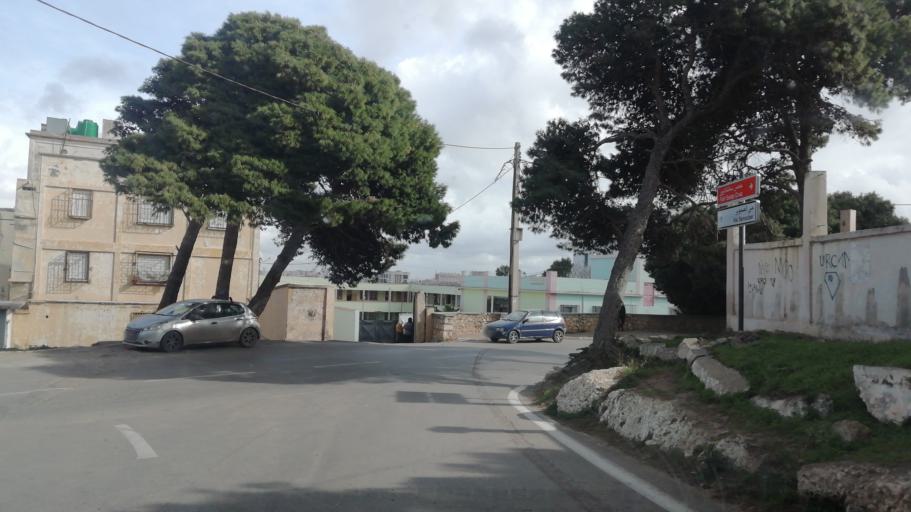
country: DZ
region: Oran
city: Oran
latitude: 35.7019
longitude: -0.6603
